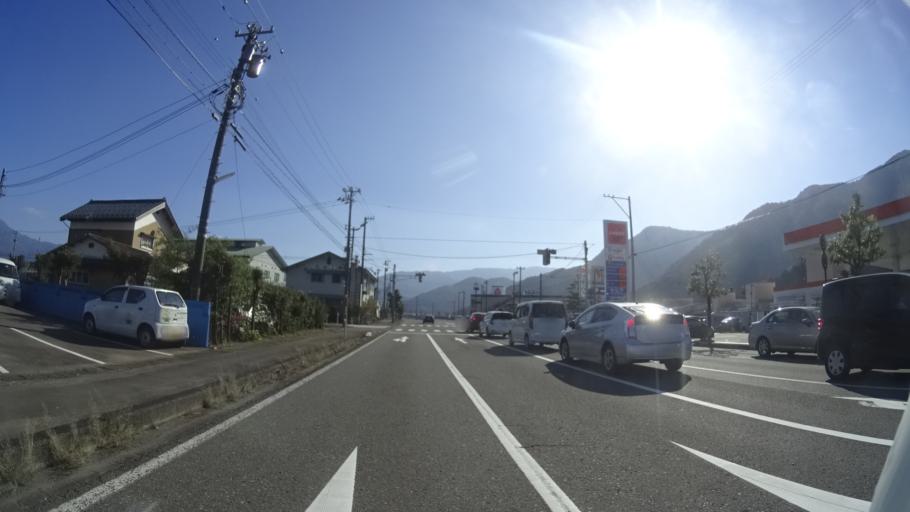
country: JP
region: Fukui
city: Ono
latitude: 35.9762
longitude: 136.4801
